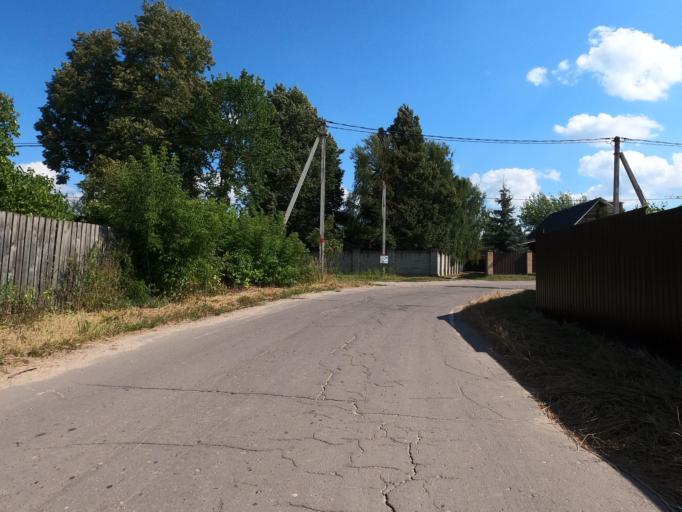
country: RU
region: Moskovskaya
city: Peski
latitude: 55.2321
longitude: 38.7494
